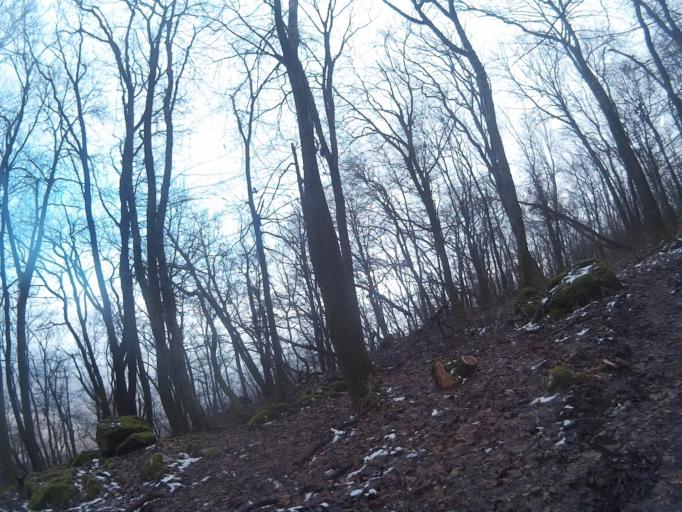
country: HU
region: Komarom-Esztergom
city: Tardos
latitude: 47.6397
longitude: 18.4791
